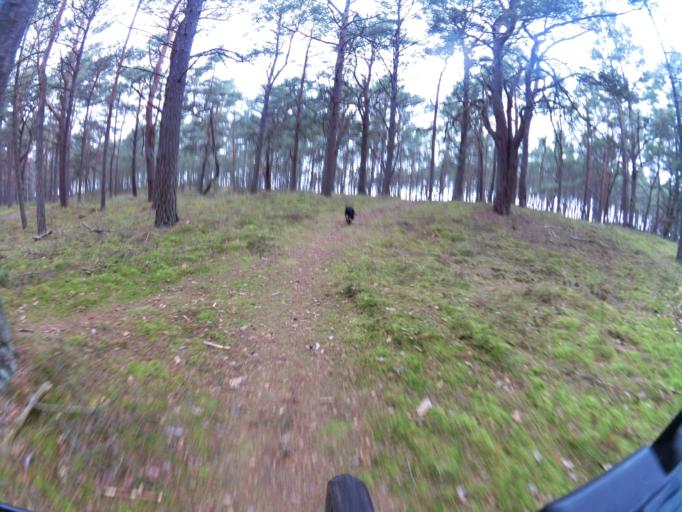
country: PL
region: West Pomeranian Voivodeship
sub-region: Powiat gryficki
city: Cerkwica
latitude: 54.1104
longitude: 15.1436
